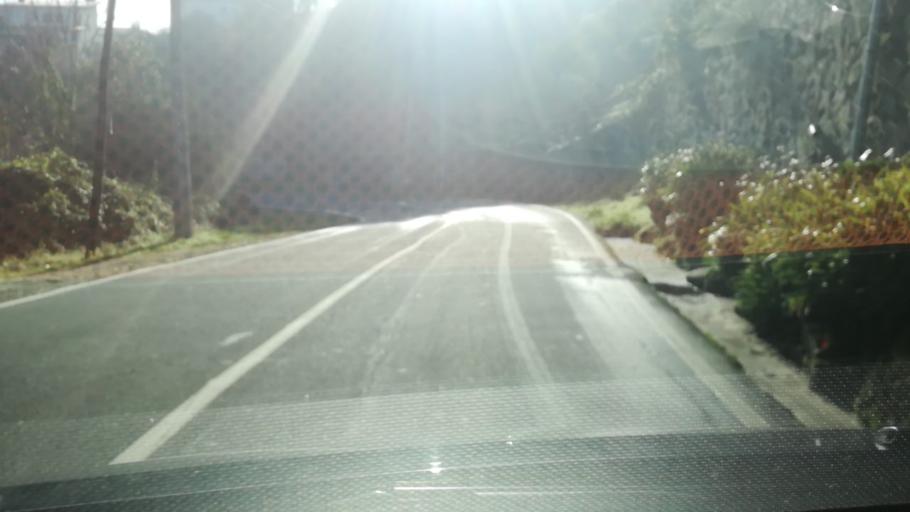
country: PT
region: Braga
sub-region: Guimaraes
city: Ponte
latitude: 41.5197
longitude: -8.3365
